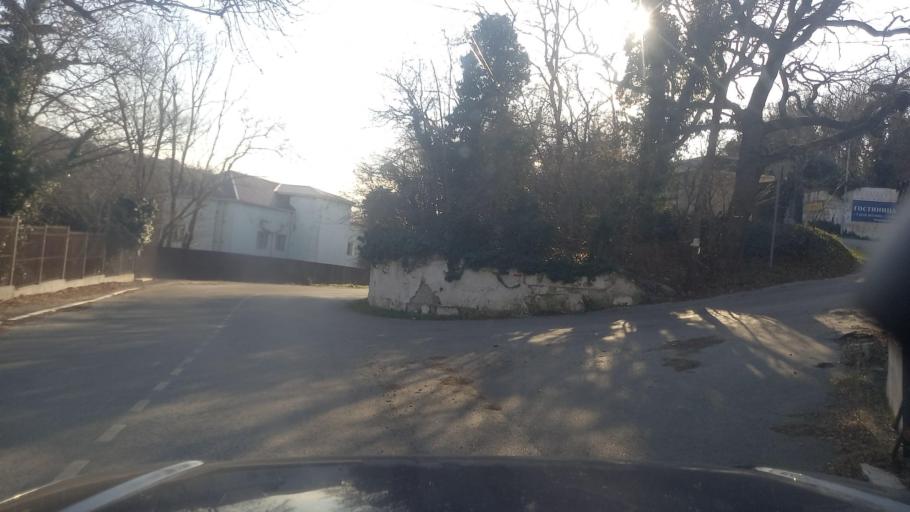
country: RU
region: Krasnodarskiy
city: Myskhako
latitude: 44.6653
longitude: 37.6851
